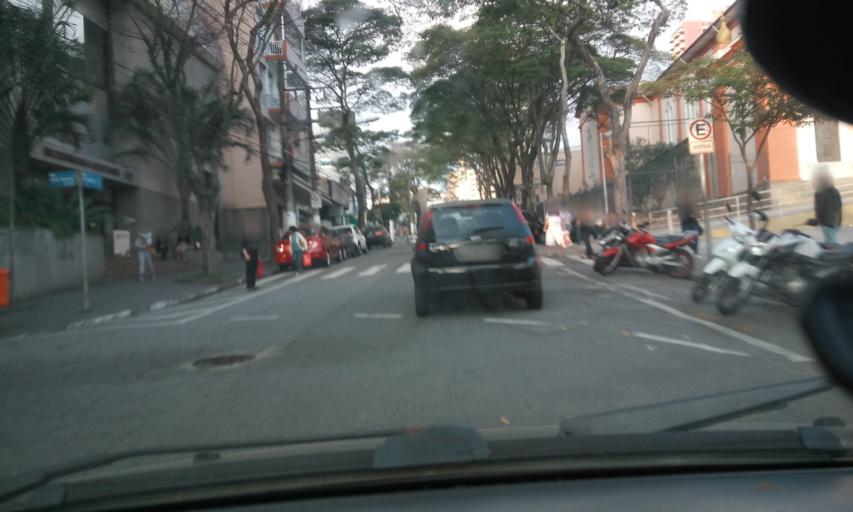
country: BR
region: Sao Paulo
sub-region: Sao Bernardo Do Campo
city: Sao Bernardo do Campo
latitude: -23.7077
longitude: -46.5505
